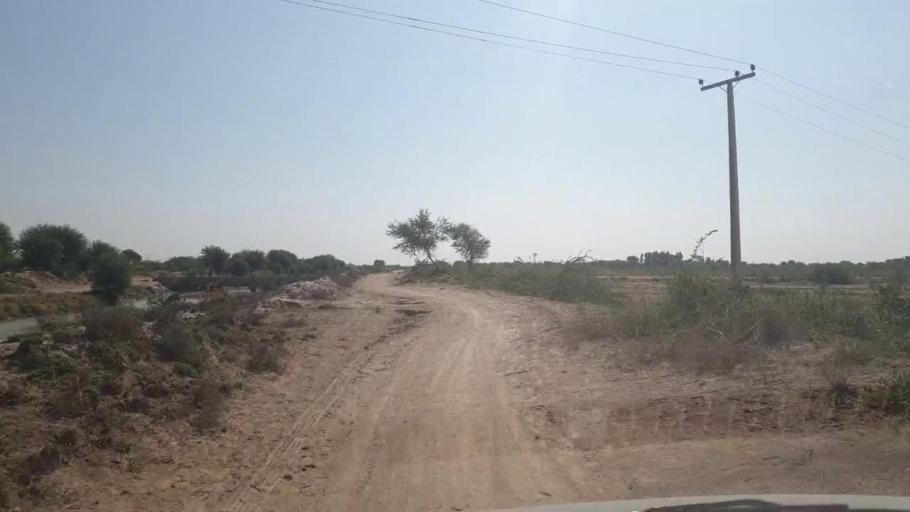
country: PK
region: Sindh
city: Digri
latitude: 24.9333
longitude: 69.1636
